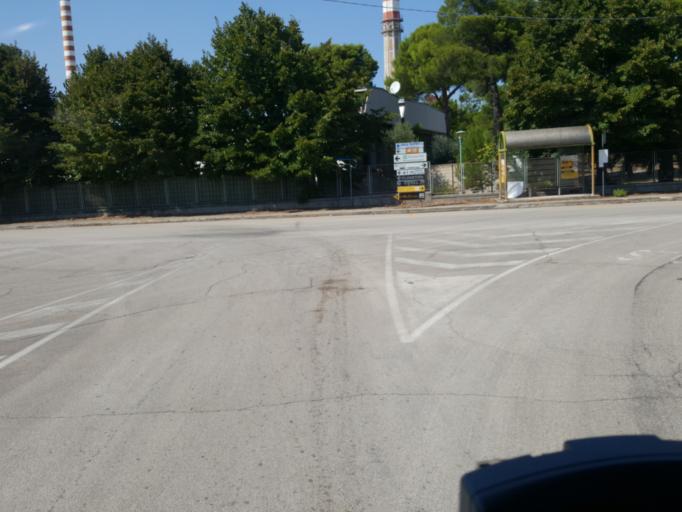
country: IT
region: Abruzzo
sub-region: Provincia di Chieti
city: Salvo Marina
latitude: 42.0574
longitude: 14.7563
